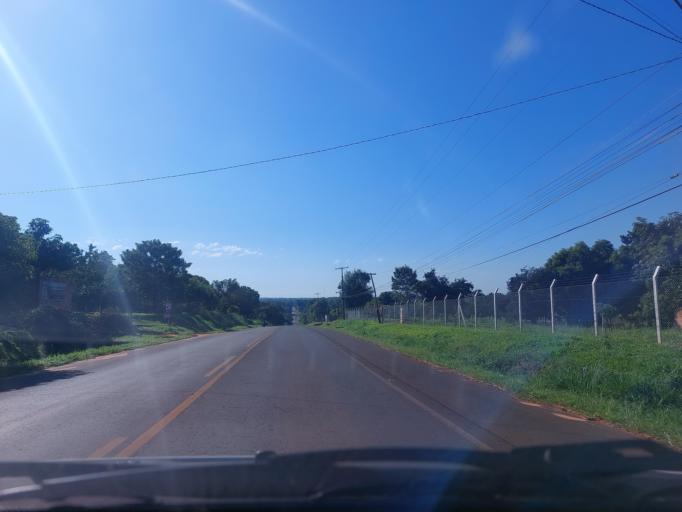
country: PY
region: San Pedro
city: Guayaybi
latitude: -24.5314
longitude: -56.4181
